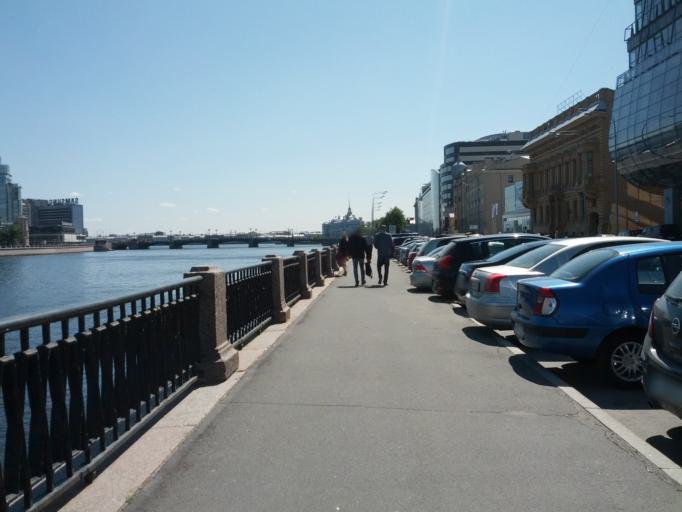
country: RU
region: St.-Petersburg
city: Petrogradka
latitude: 59.9628
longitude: 30.3348
